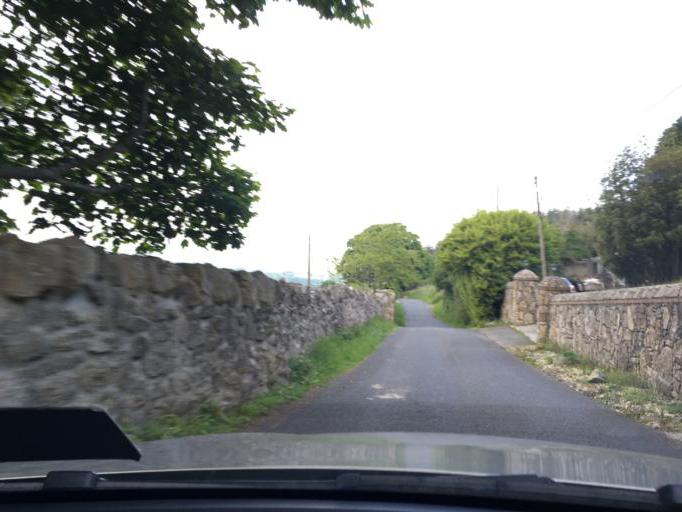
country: IE
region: Leinster
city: Ballinteer
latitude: 53.2559
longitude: -6.2782
